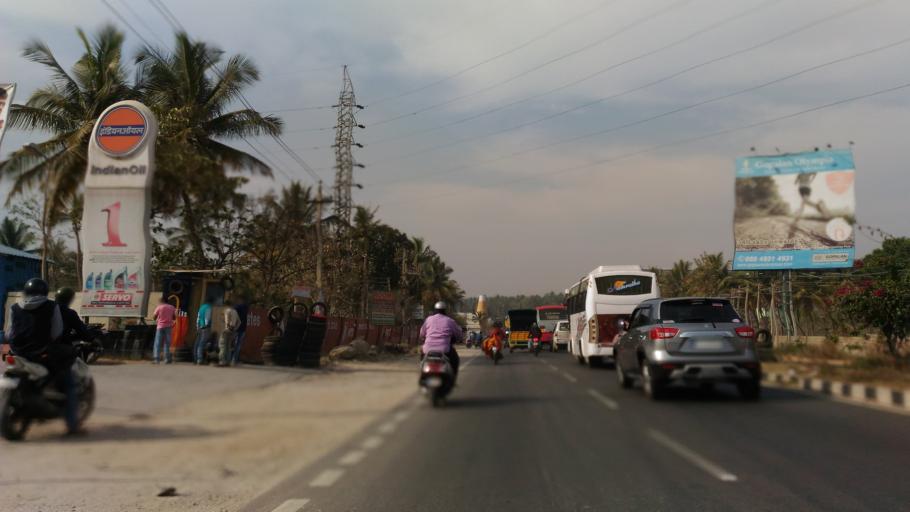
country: IN
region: Karnataka
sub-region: Bangalore Urban
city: Bangalore
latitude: 12.8737
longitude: 77.4418
